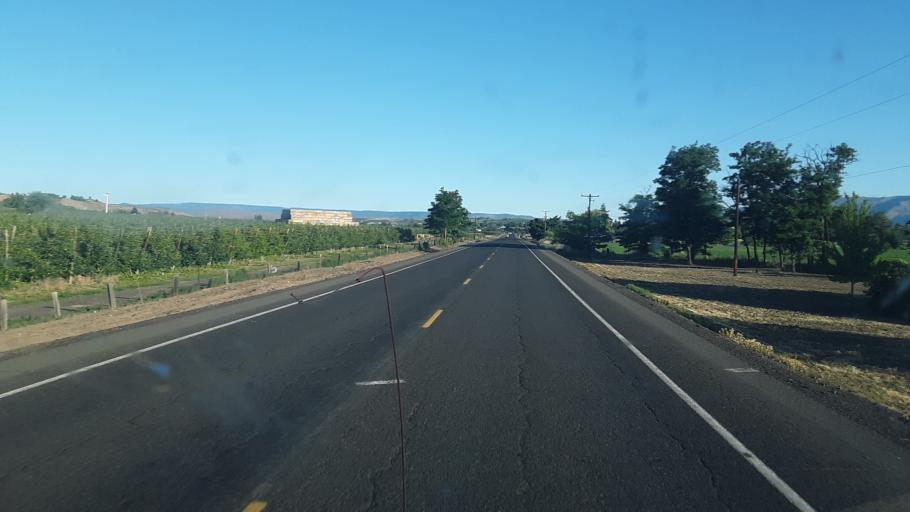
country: US
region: Washington
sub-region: Yakima County
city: Gleed
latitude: 46.6392
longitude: -120.6859
